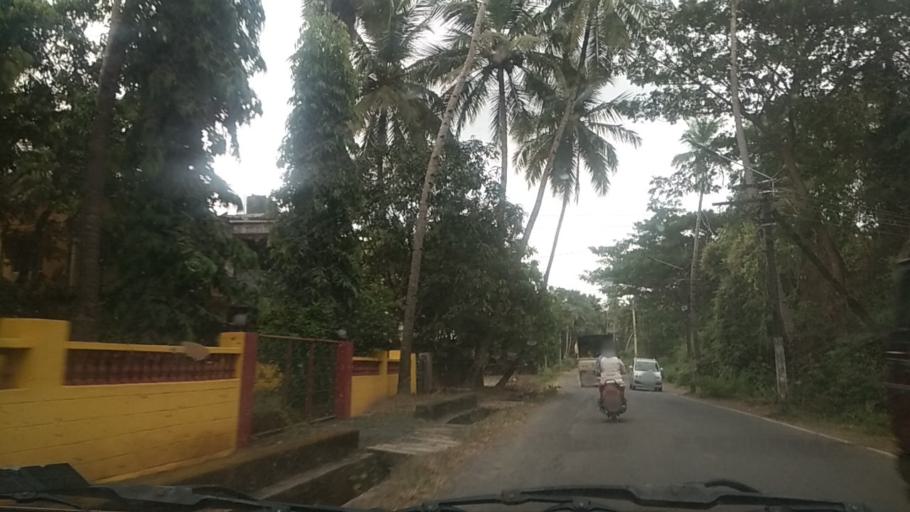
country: IN
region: Goa
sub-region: South Goa
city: Chinchinim
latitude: 15.2039
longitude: 73.9772
